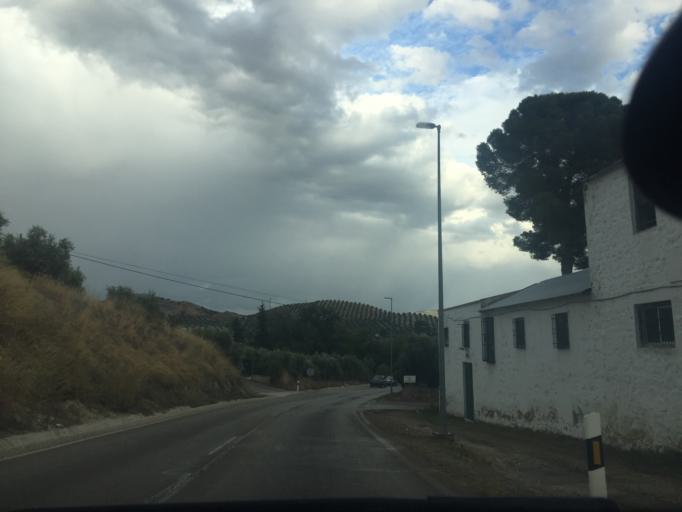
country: ES
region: Andalusia
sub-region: Provincia de Jaen
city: Jaen
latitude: 37.7614
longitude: -3.7593
